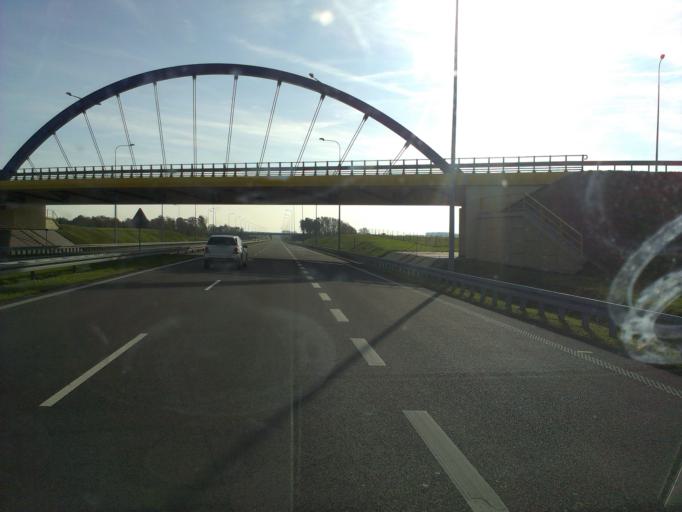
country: PL
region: West Pomeranian Voivodeship
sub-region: Powiat pyrzycki
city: Bielice
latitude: 53.1235
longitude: 14.7384
